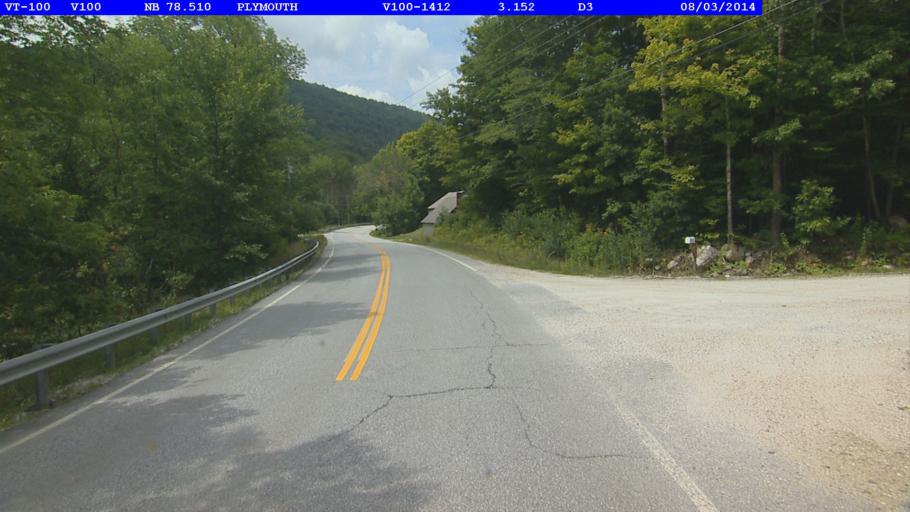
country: US
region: Vermont
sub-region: Windsor County
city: Woodstock
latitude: 43.5025
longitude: -72.7232
